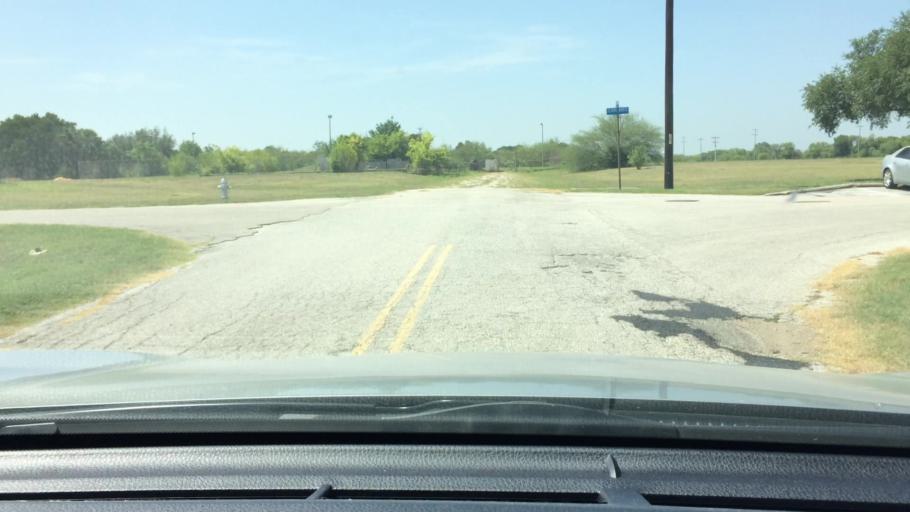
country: US
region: Texas
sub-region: Bexar County
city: San Antonio
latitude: 29.3404
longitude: -98.4501
